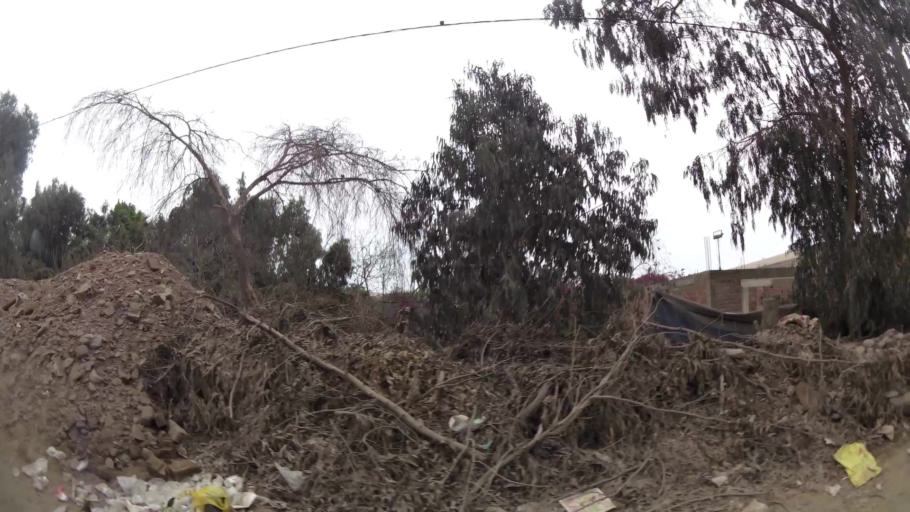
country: PE
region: Lima
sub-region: Lima
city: Surco
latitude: -12.2128
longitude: -76.9669
